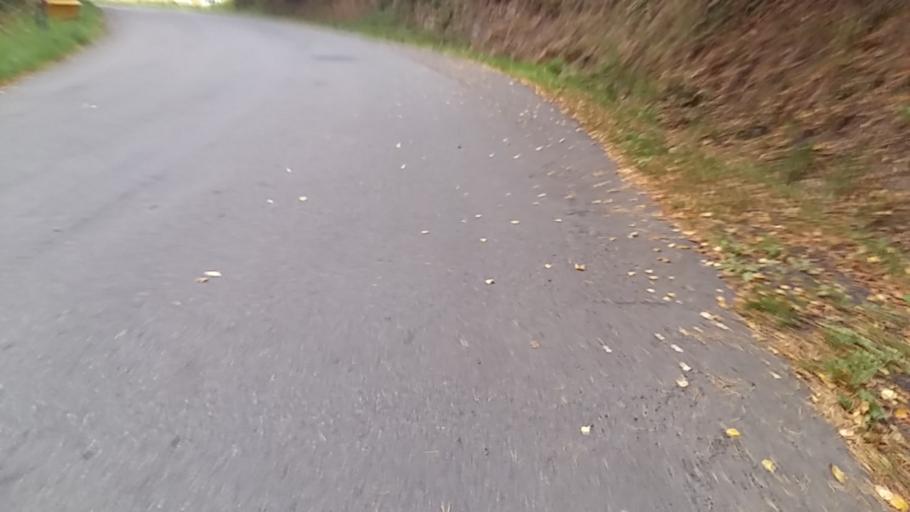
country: SE
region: Joenkoeping
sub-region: Jonkopings Kommun
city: Taberg
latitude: 57.7040
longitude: 14.1126
